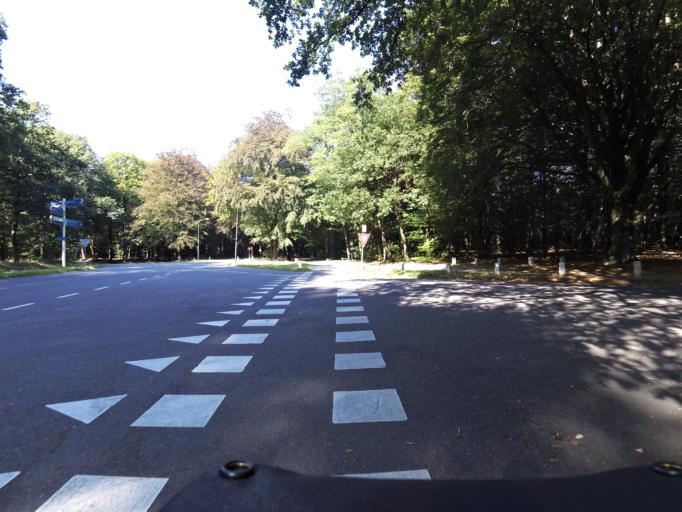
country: NL
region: Gelderland
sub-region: Gemeente Apeldoorn
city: Apeldoorn
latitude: 52.2193
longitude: 5.9109
